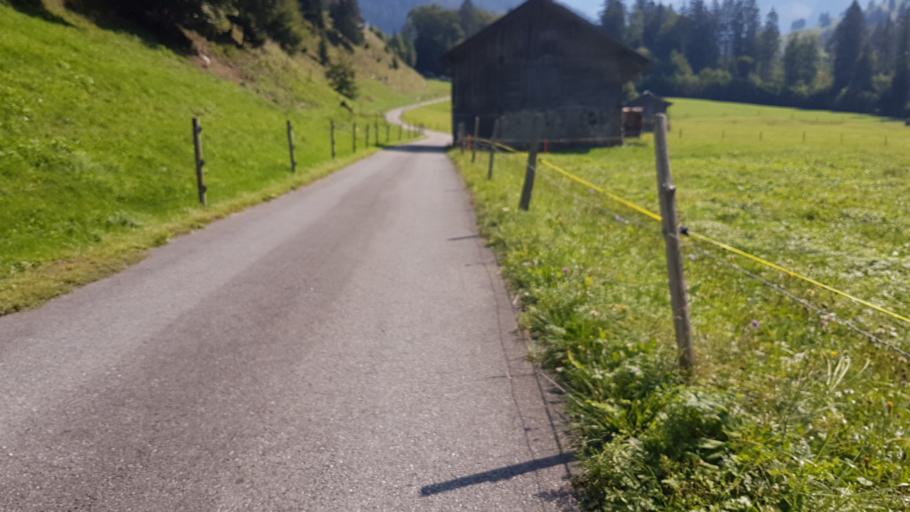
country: CH
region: Bern
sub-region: Frutigen-Niedersimmental District
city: Frutigen
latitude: 46.5892
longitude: 7.7207
